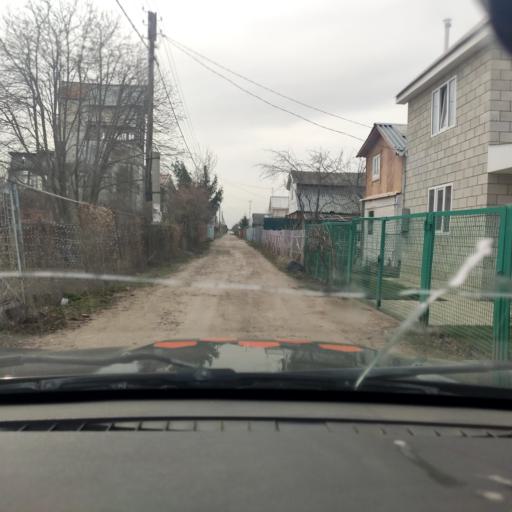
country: RU
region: Samara
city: Tol'yatti
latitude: 53.6019
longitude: 49.2471
